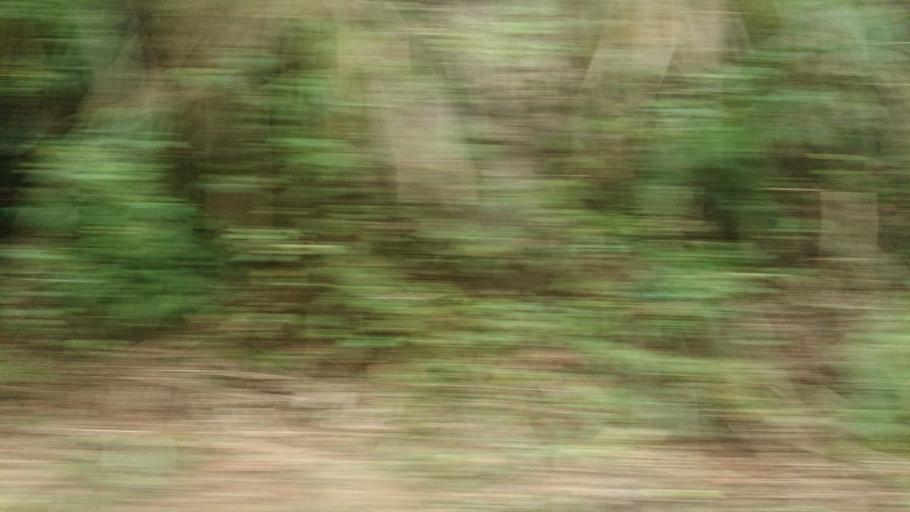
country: TW
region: Taiwan
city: Lugu
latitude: 23.6289
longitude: 120.7173
